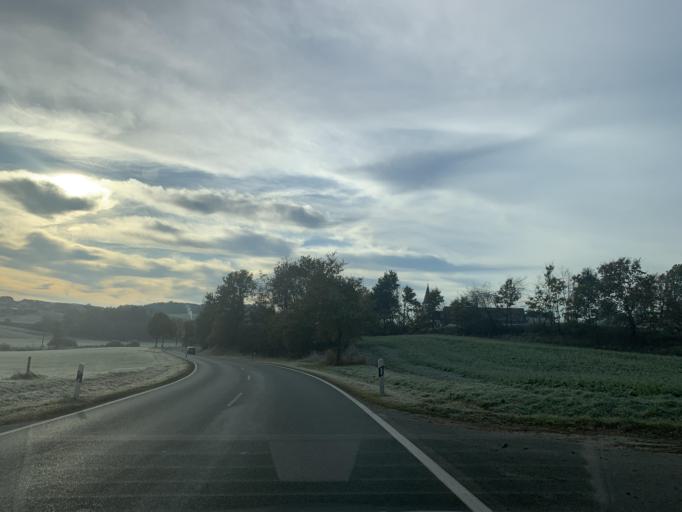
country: DE
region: Bavaria
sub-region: Upper Palatinate
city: Pettendorf
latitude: 49.3737
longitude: 12.3767
